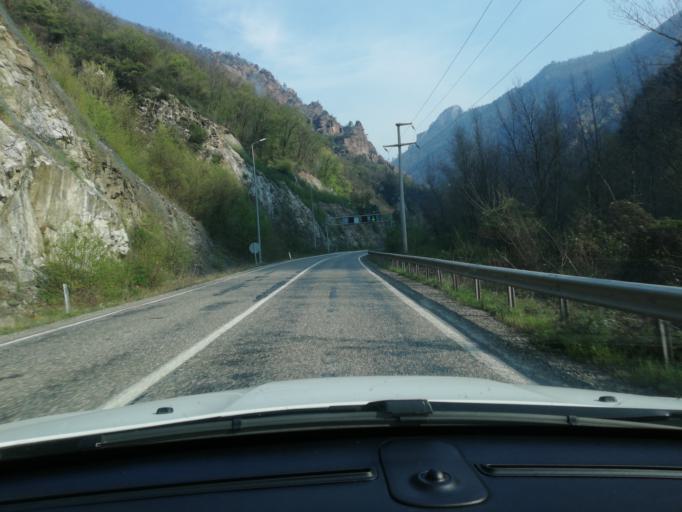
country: TR
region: Karabuk
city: Yenice
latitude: 41.1742
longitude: 32.4465
